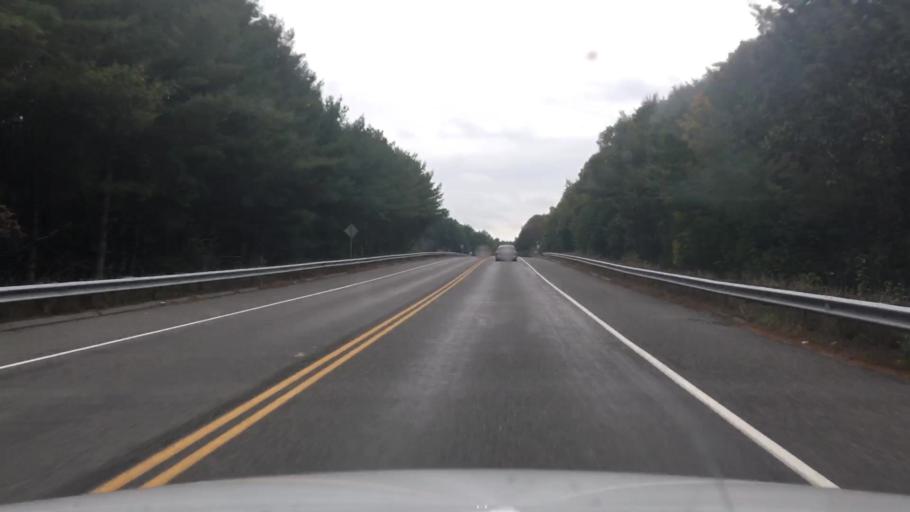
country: US
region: New Hampshire
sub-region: Carroll County
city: Wolfeboro
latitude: 43.4961
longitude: -71.2582
